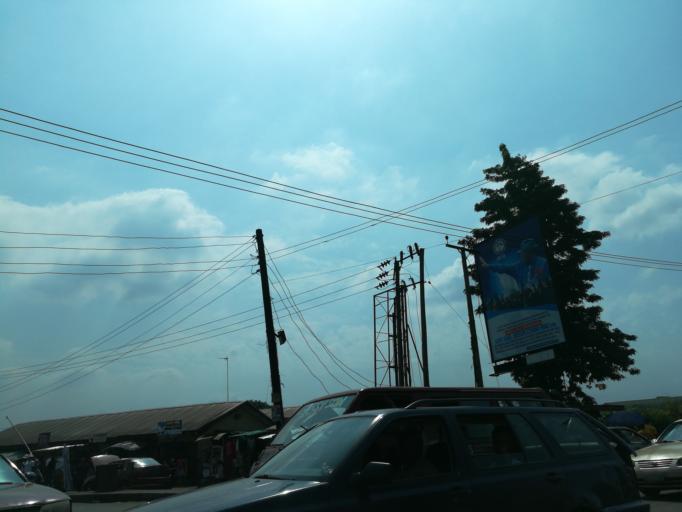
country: NG
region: Rivers
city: Port Harcourt
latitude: 4.8274
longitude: 6.9814
